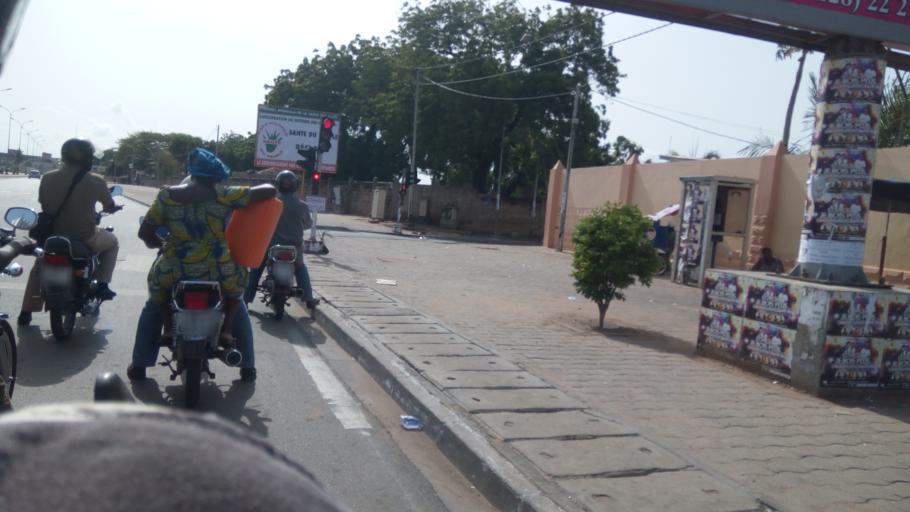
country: TG
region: Maritime
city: Lome
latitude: 6.1370
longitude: 1.2253
